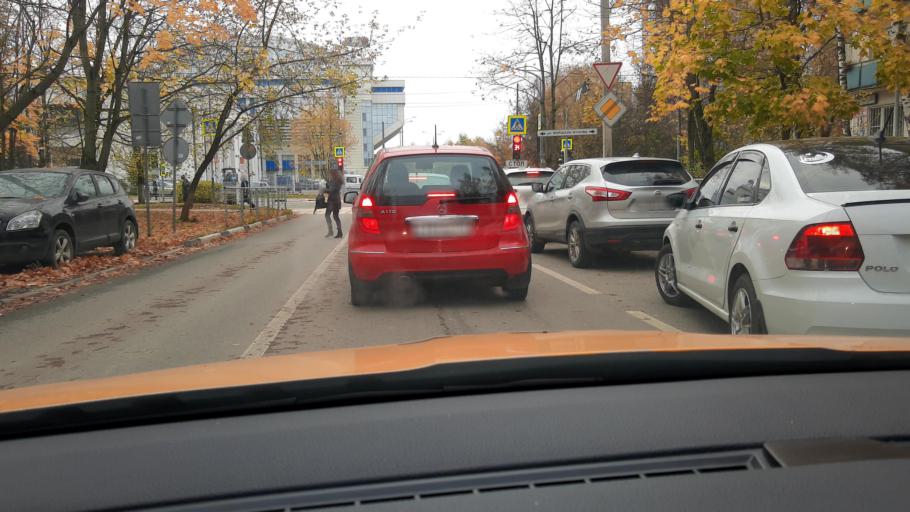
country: RU
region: Moskovskaya
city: Odintsovo
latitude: 55.6791
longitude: 37.2580
